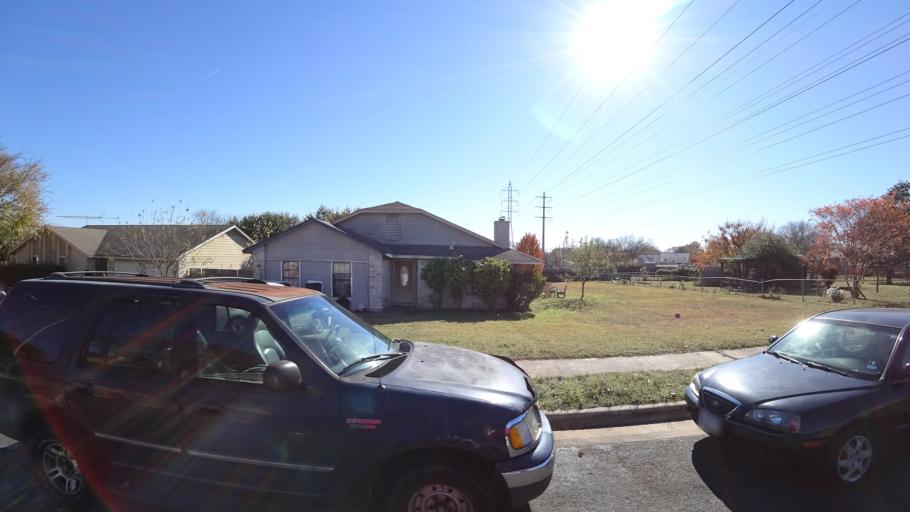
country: US
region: Texas
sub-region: Travis County
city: Wells Branch
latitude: 30.4224
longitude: -97.6883
